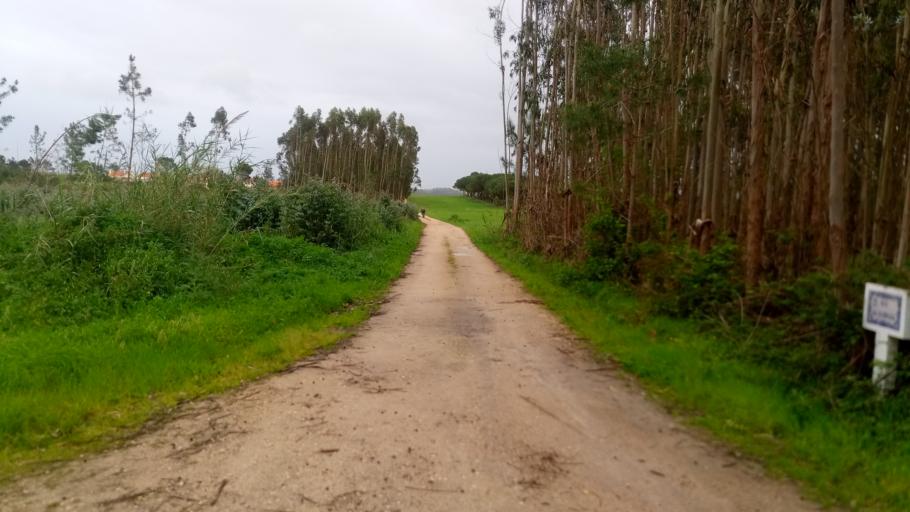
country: PT
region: Leiria
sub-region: Caldas da Rainha
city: Caldas da Rainha
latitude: 39.4442
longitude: -9.1561
